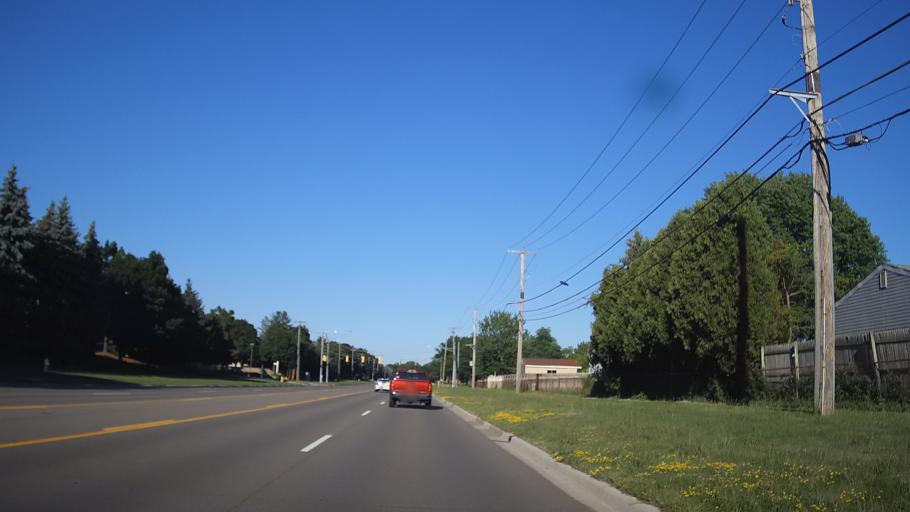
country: US
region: Michigan
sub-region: Macomb County
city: Clinton
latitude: 42.6132
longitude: -82.9436
